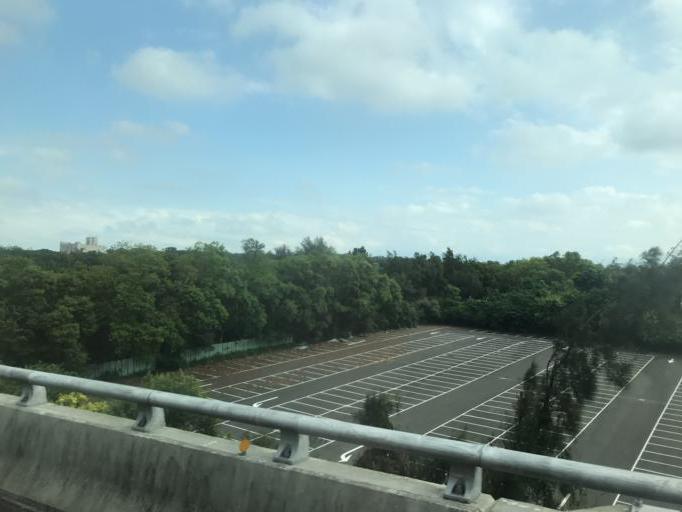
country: TW
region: Taiwan
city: Daxi
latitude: 24.9279
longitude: 121.1751
